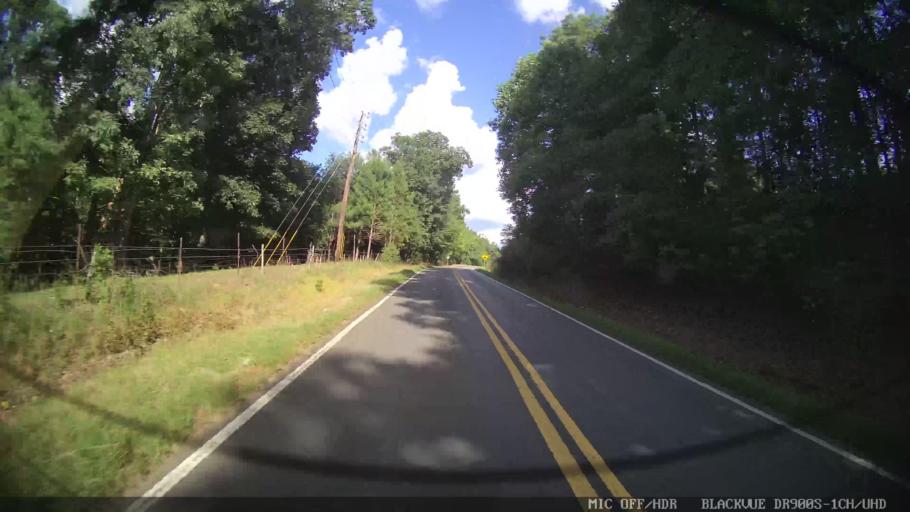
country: US
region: Georgia
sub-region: Floyd County
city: Lindale
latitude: 34.2027
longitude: -85.1160
